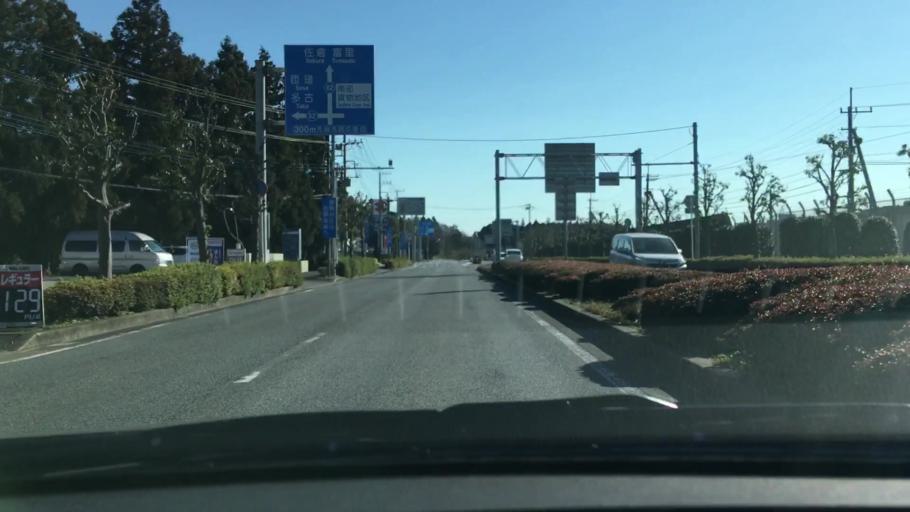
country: JP
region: Chiba
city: Narita
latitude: 35.7479
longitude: 140.4019
